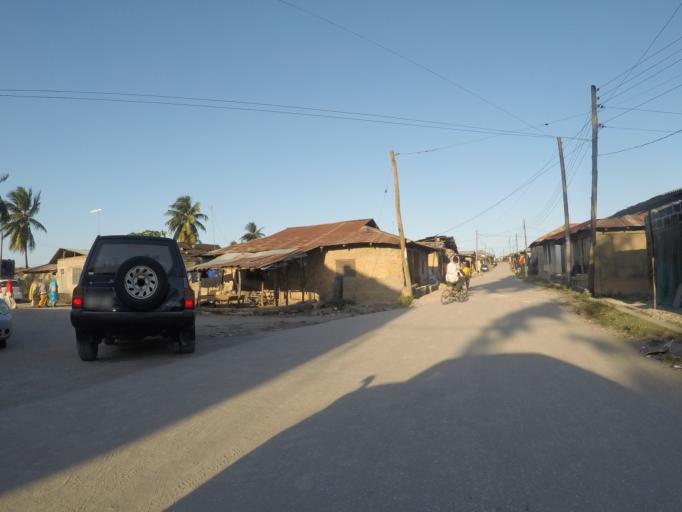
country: TZ
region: Zanzibar Urban/West
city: Zanzibar
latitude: -6.1575
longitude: 39.2103
